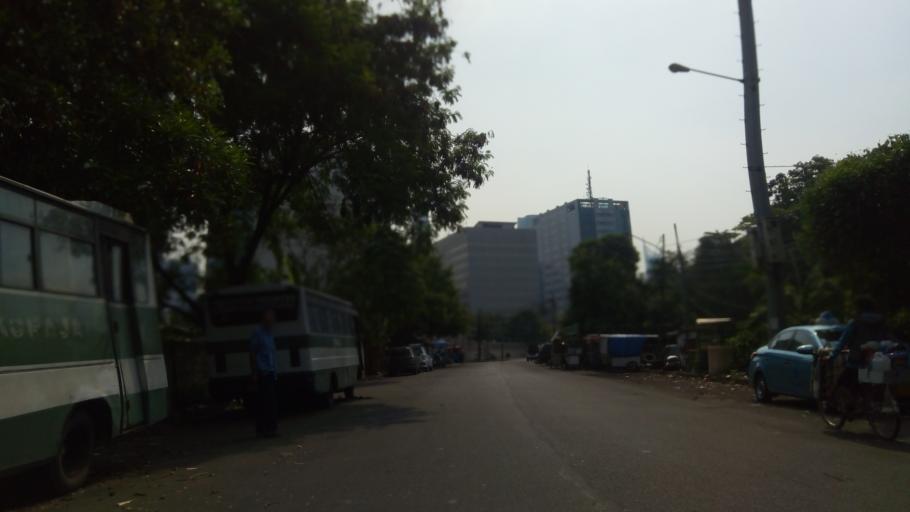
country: ID
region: Jakarta Raya
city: Jakarta
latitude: -6.2125
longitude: 106.8325
